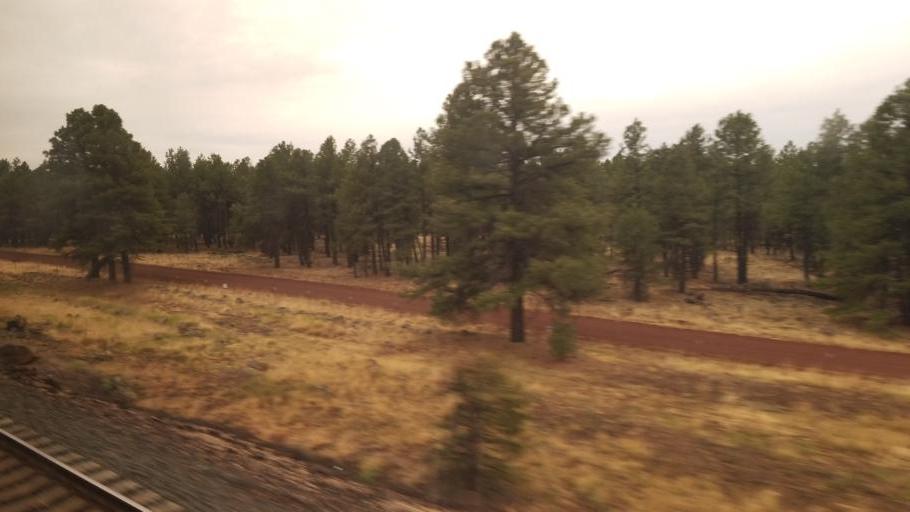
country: US
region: Arizona
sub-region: Coconino County
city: Flagstaff
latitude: 35.2175
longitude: -111.7908
